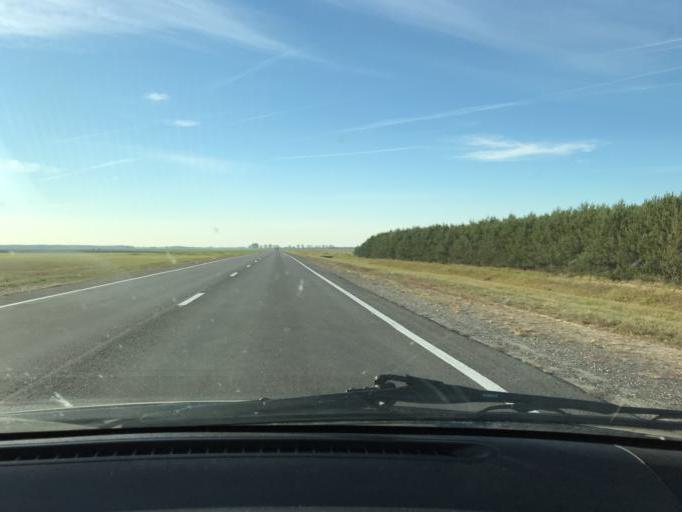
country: BY
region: Brest
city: Antopal'
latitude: 52.2220
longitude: 24.8368
